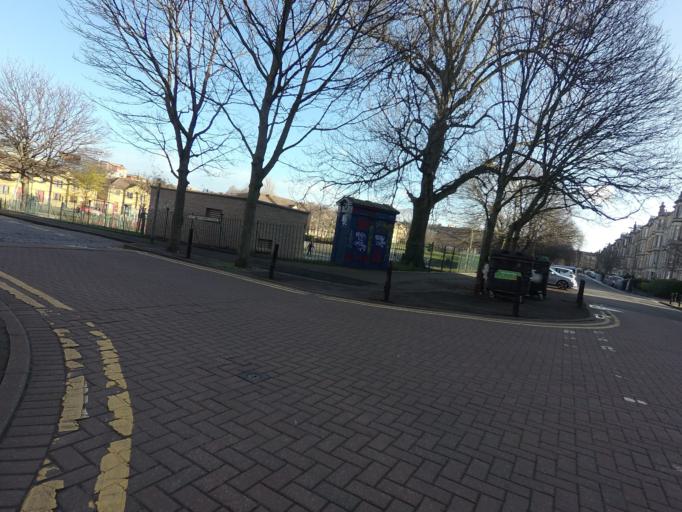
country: GB
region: Scotland
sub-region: Edinburgh
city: Edinburgh
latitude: 55.9593
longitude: -3.1767
